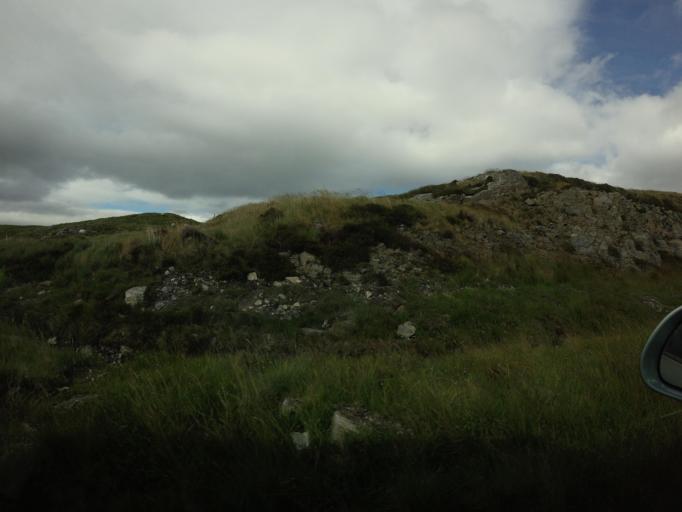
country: GB
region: Scotland
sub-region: Eilean Siar
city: Harris
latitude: 58.1942
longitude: -6.7159
